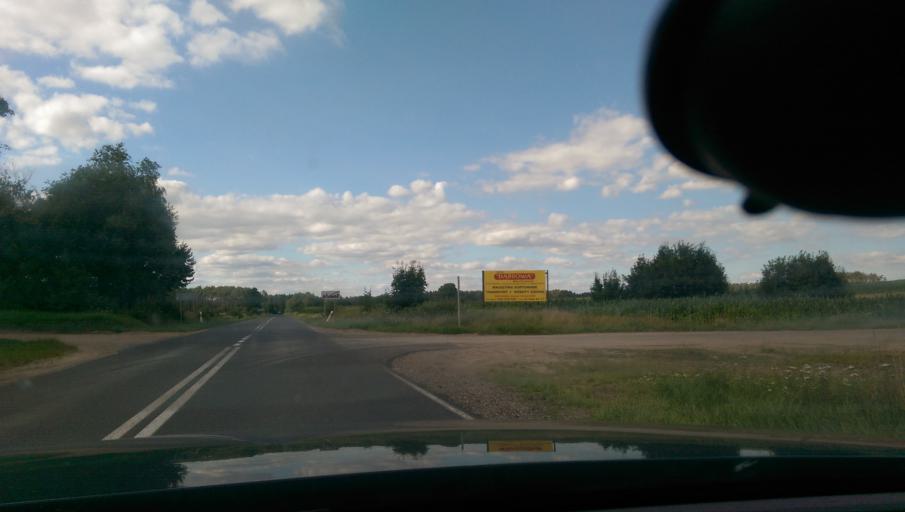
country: PL
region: Lubusz
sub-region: Powiat slubicki
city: Osno Lubuskie
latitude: 52.4995
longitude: 14.9103
